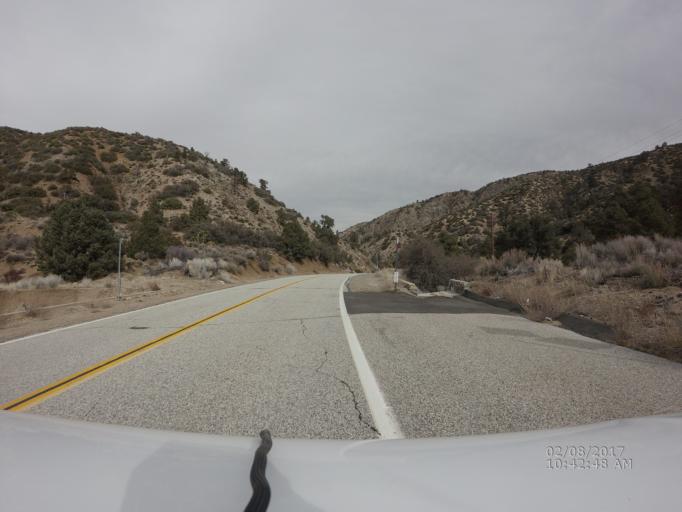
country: US
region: California
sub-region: San Bernardino County
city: Pinon Hills
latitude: 34.4221
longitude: -117.7676
